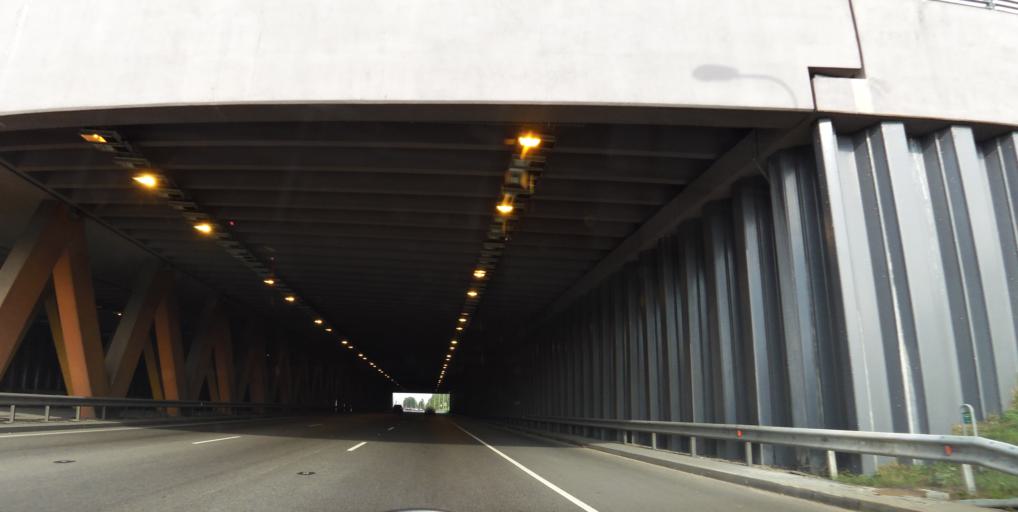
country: LT
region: Vilnius County
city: Lazdynai
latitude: 54.6741
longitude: 25.1964
